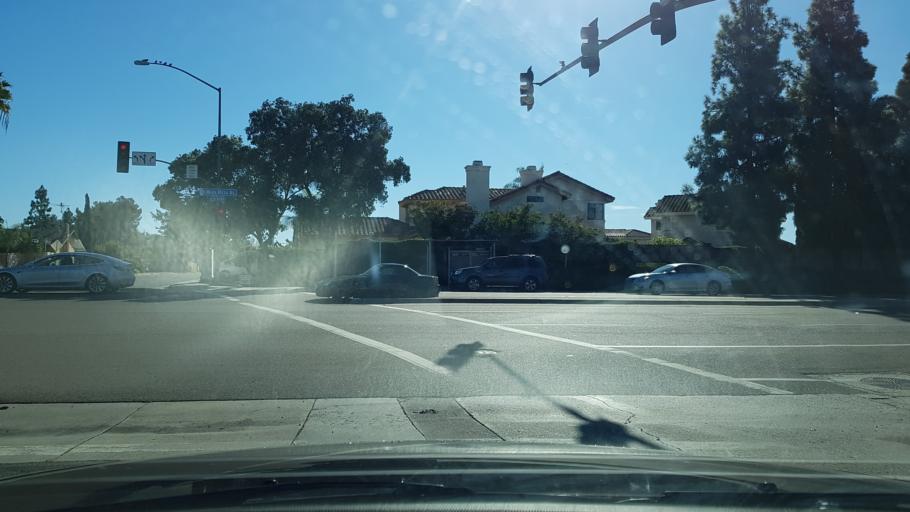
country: US
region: California
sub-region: San Diego County
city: Fairbanks Ranch
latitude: 32.9131
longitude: -117.1358
